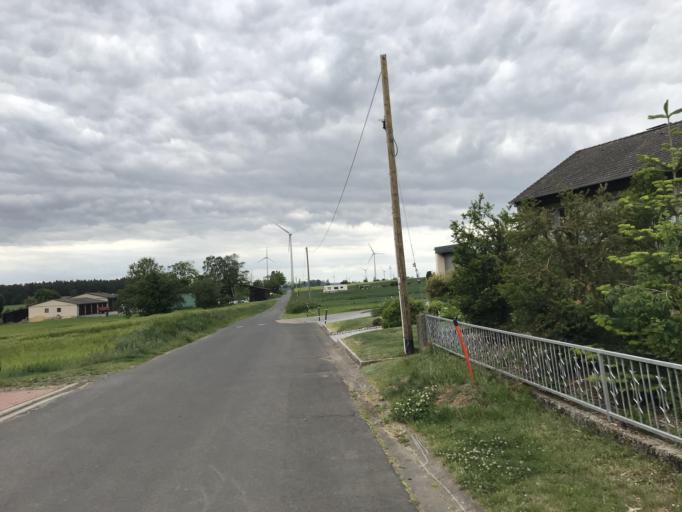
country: DE
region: Hesse
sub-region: Regierungsbezirk Kassel
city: Martinhagen
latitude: 51.2885
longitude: 9.2795
